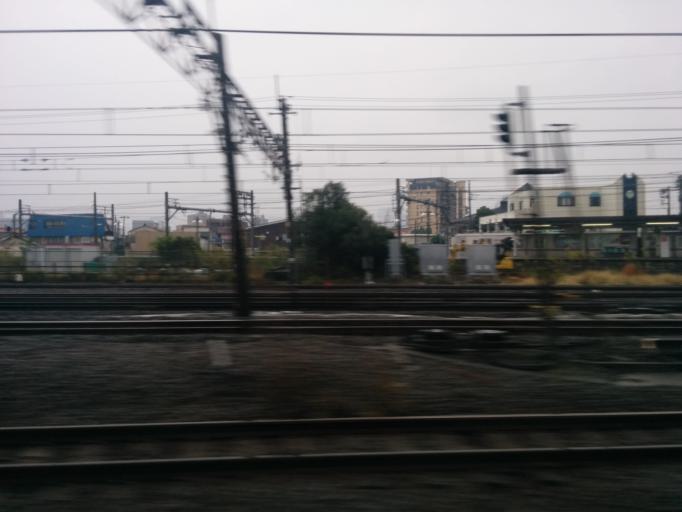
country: JP
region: Chiba
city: Funabashi
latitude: 35.6609
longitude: 140.0565
